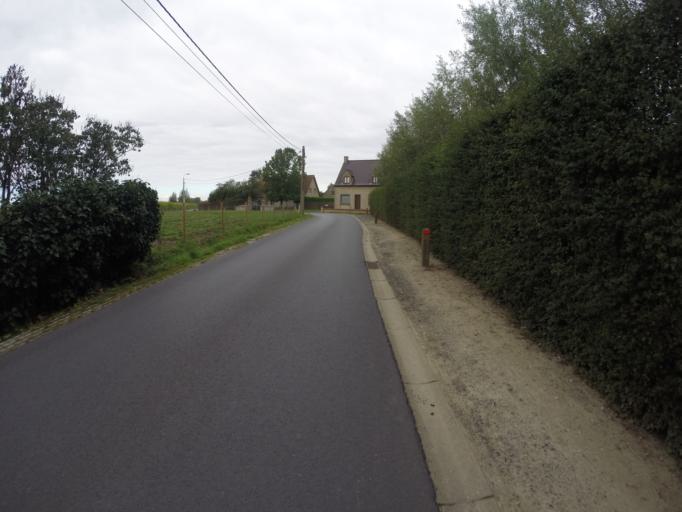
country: BE
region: Flanders
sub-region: Provincie West-Vlaanderen
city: Ruiselede
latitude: 51.0427
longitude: 3.3812
